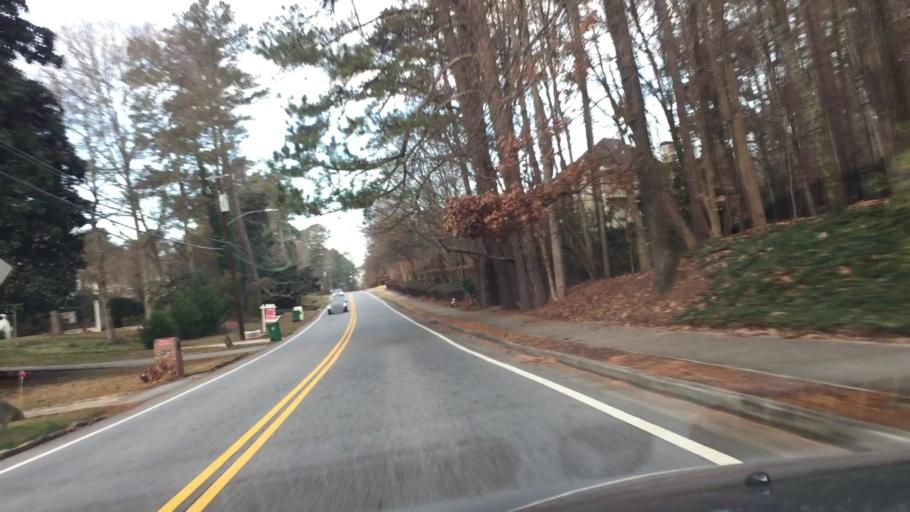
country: US
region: Georgia
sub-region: DeKalb County
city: Dunwoody
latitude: 33.9688
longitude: -84.3301
